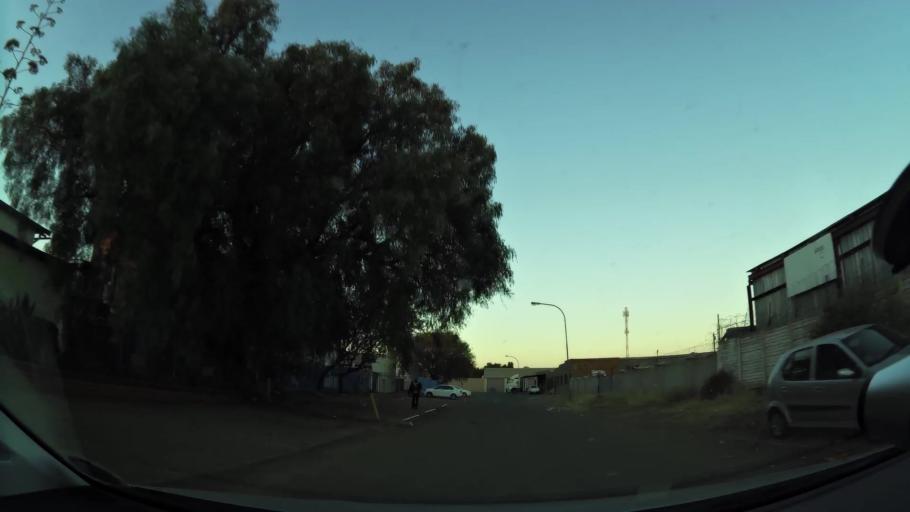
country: ZA
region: Northern Cape
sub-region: Frances Baard District Municipality
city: Kimberley
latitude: -28.7290
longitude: 24.7741
